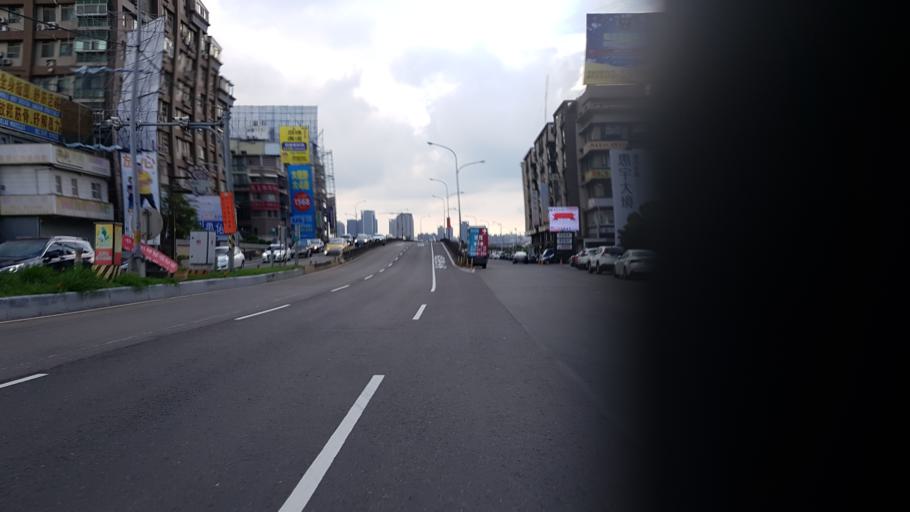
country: TW
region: Taiwan
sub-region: Hsinchu
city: Zhubei
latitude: 24.8121
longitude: 121.0224
